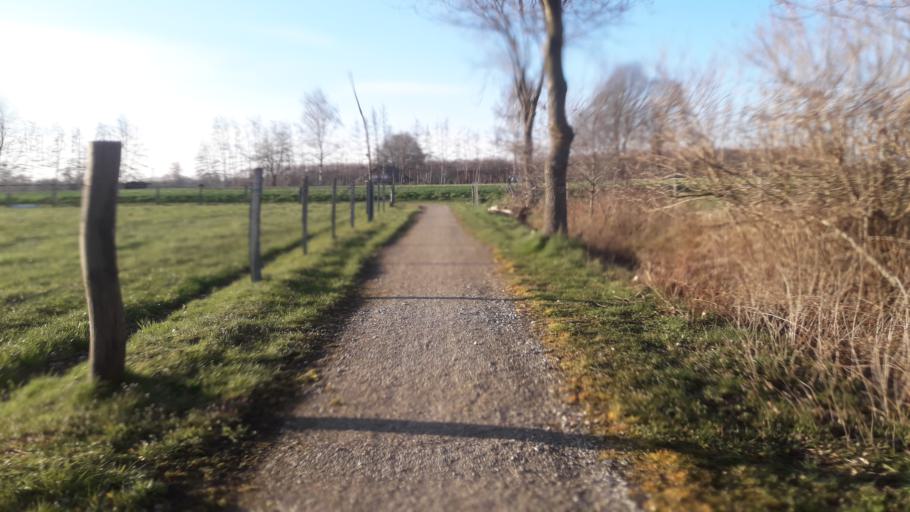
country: DE
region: North Rhine-Westphalia
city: Rietberg
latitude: 51.7832
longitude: 8.4799
